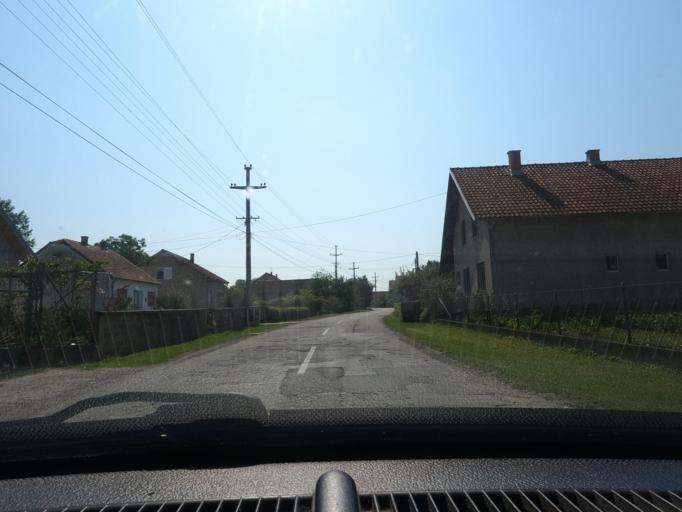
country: RS
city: Lipnicki Sor
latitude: 44.5790
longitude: 19.2689
